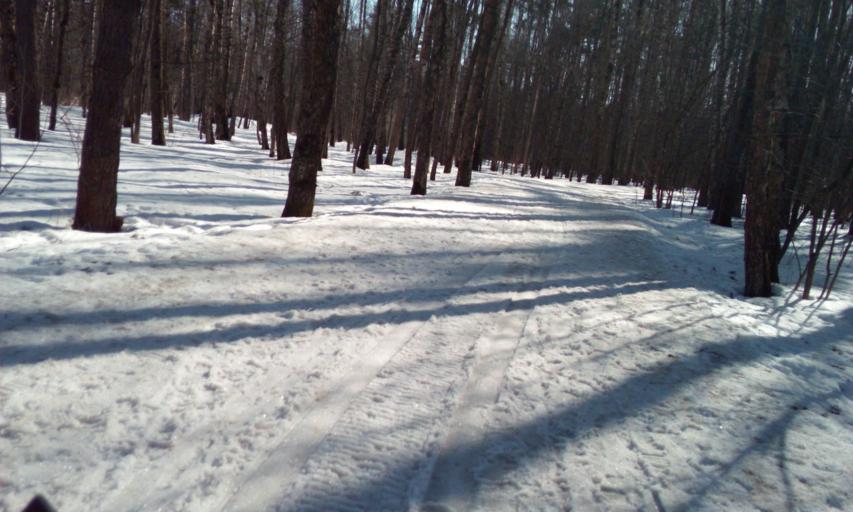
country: RU
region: Moskovskaya
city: Skolkovo
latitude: 55.6667
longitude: 37.3786
